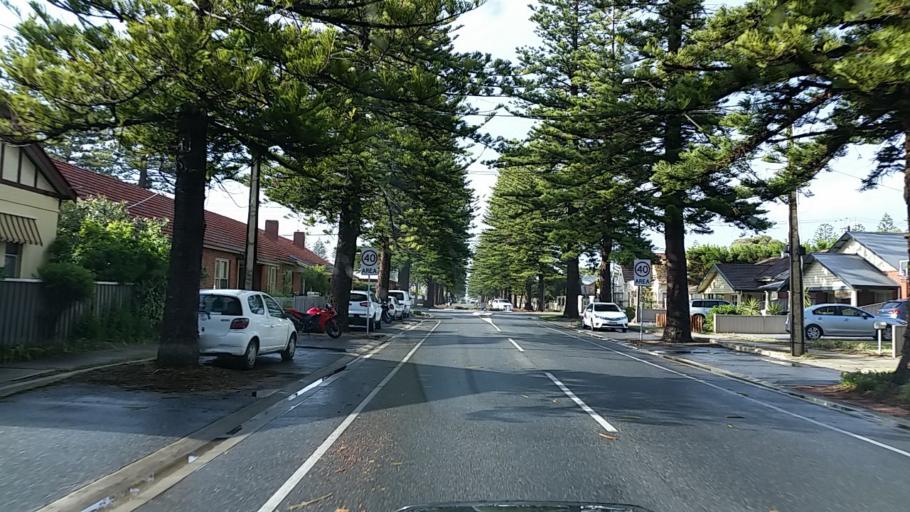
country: AU
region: South Australia
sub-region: Charles Sturt
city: Henley Beach
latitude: -34.9229
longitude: 138.4975
